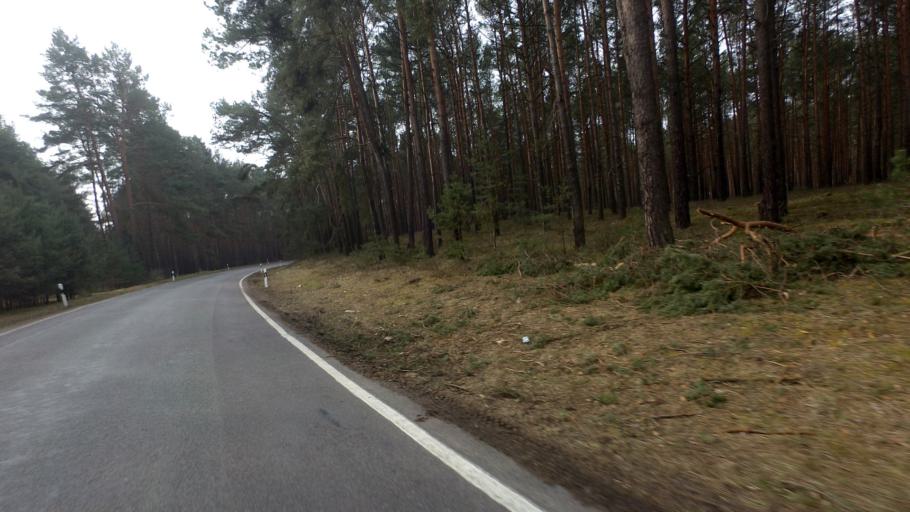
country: DE
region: Brandenburg
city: Borkheide
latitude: 52.1978
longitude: 12.8679
